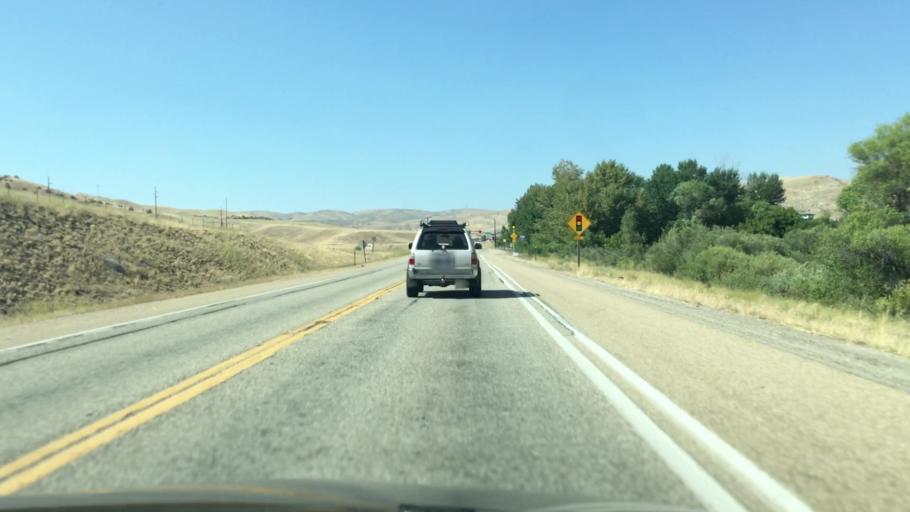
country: US
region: Idaho
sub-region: Ada County
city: Eagle
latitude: 43.7705
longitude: -116.2659
